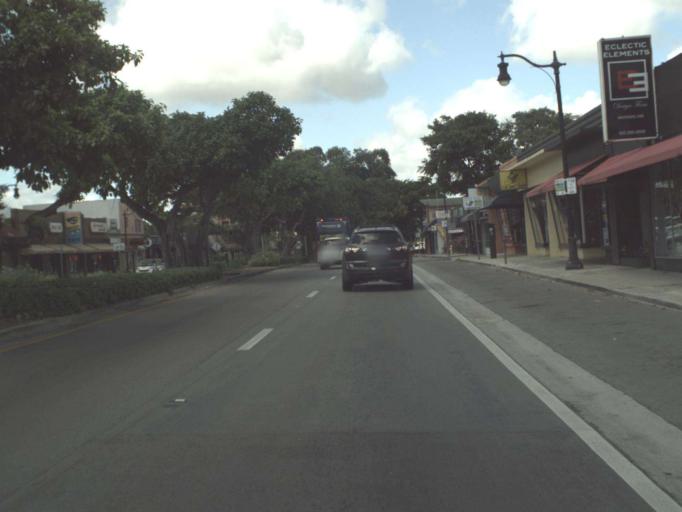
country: US
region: Florida
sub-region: Miami-Dade County
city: Miami
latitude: 25.7507
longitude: -80.2306
